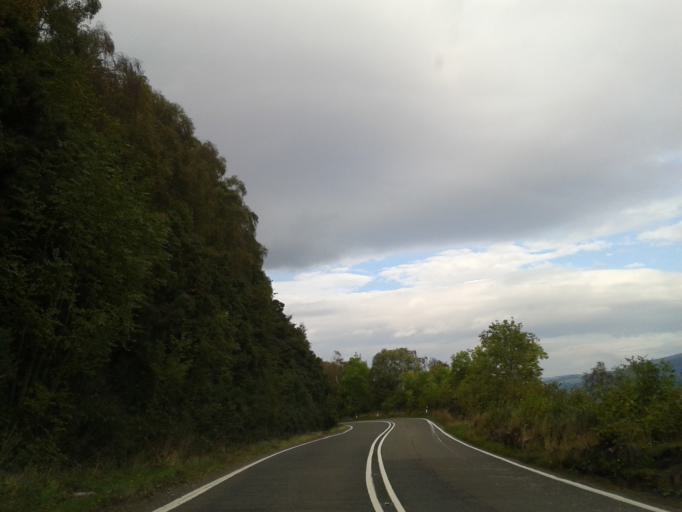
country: GB
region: Scotland
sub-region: Highland
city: Beauly
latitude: 57.3204
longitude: -4.4478
